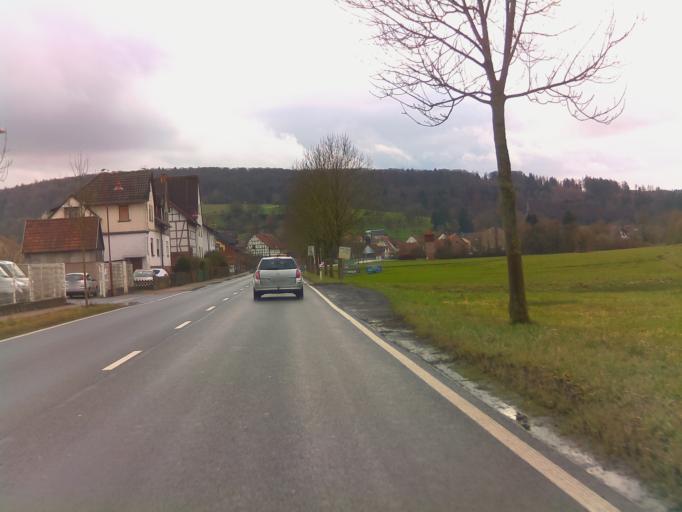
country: DE
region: Hesse
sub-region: Regierungsbezirk Darmstadt
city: Wachtersbach
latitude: 50.2251
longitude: 9.2723
